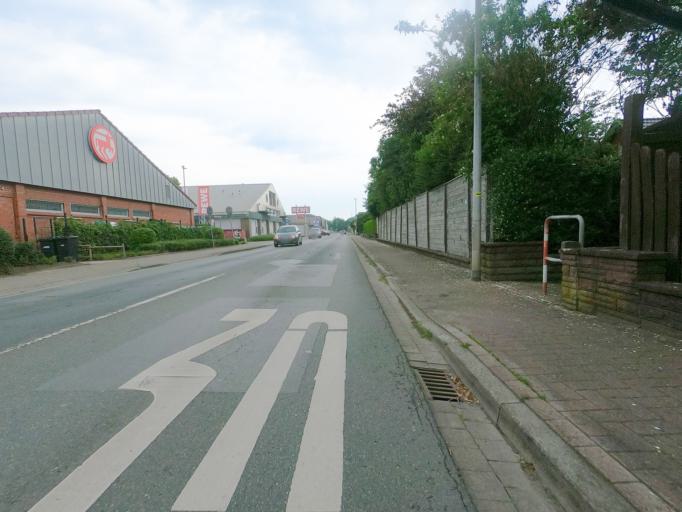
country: DE
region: Lower Saxony
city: Syke
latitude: 52.9803
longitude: 8.8517
